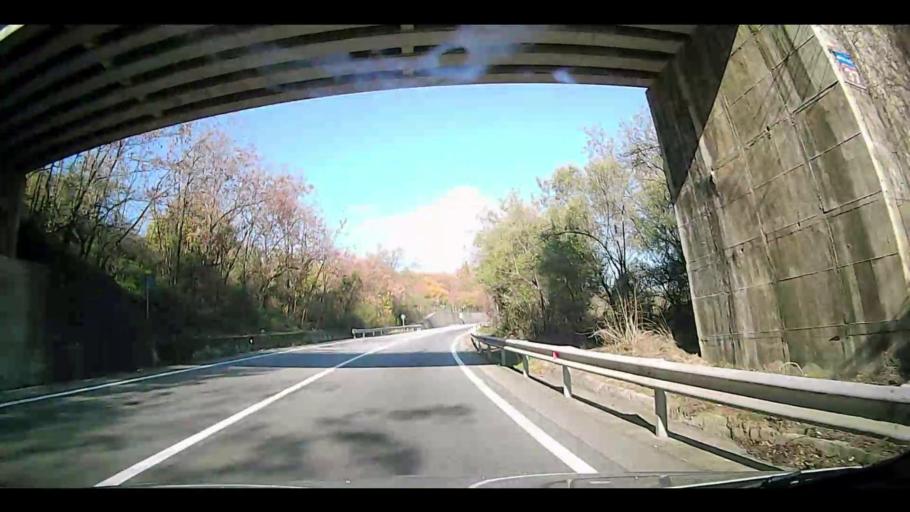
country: IT
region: Calabria
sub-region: Provincia di Crotone
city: Caccuri
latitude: 39.2041
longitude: 16.8068
